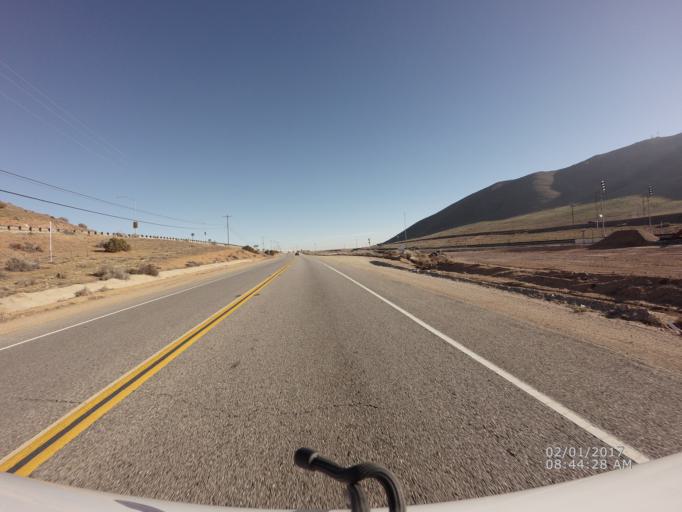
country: US
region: California
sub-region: Los Angeles County
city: Vincent
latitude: 34.5056
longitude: -118.1138
